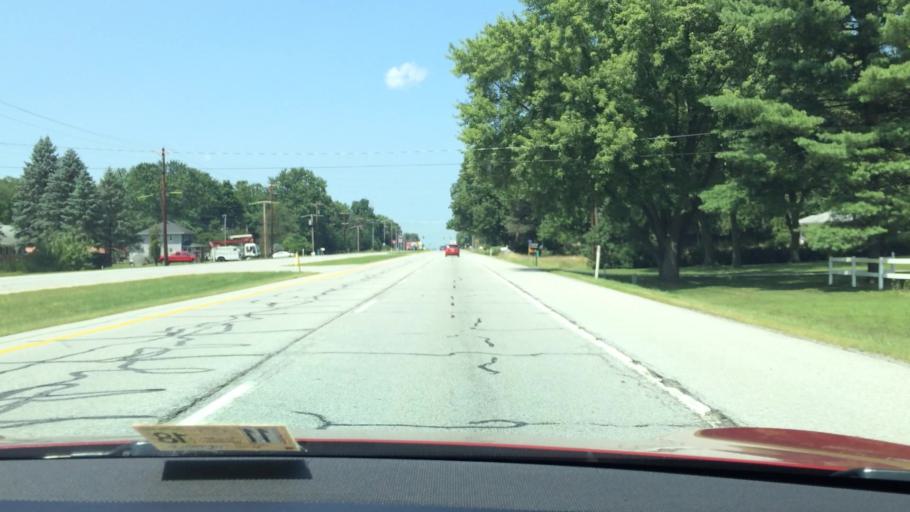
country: US
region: Indiana
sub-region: Saint Joseph County
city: South Bend
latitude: 41.6720
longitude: -86.3750
